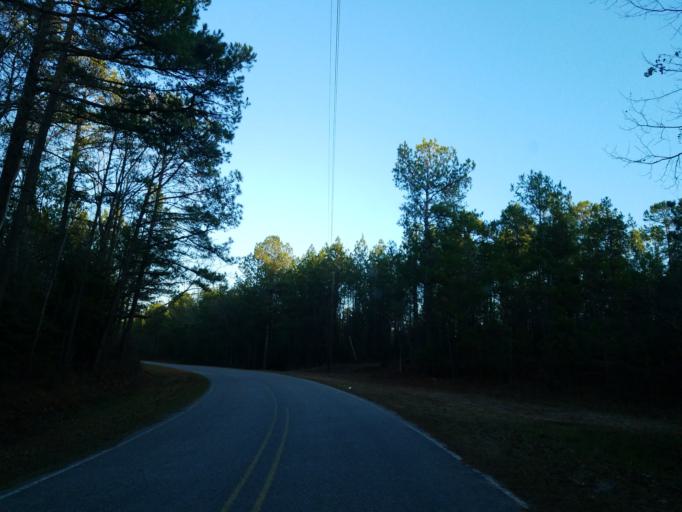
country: US
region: Mississippi
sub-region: Clarke County
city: Stonewall
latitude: 32.2620
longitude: -88.8079
